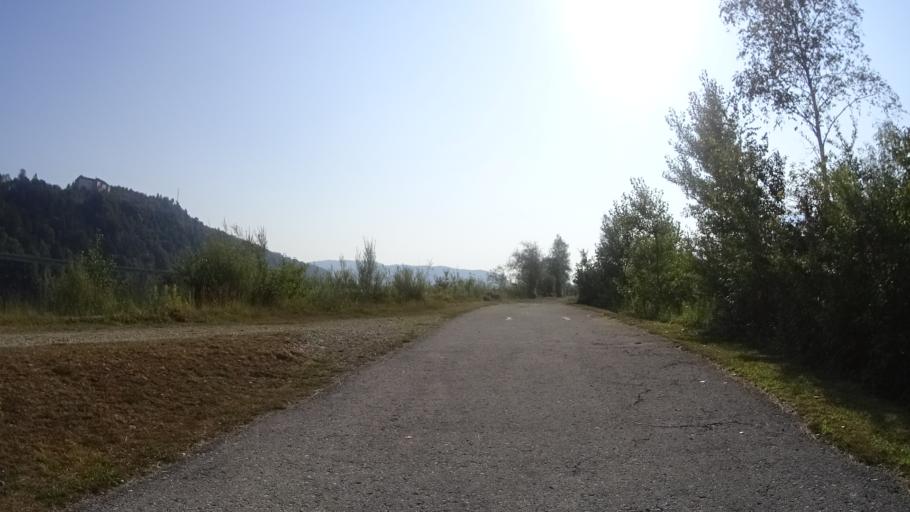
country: AT
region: Carinthia
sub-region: Politischer Bezirk Klagenfurt Land
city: Kottmannsdorf
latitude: 46.5415
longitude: 14.2558
